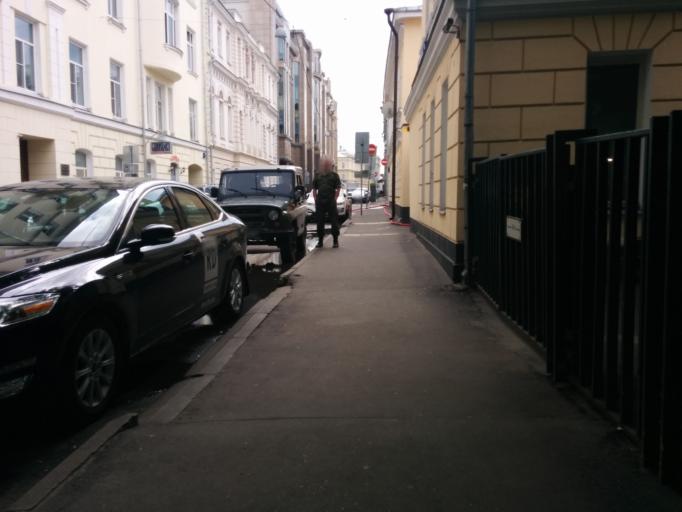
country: RU
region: Moscow
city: Moscow
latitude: 55.7545
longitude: 37.6063
